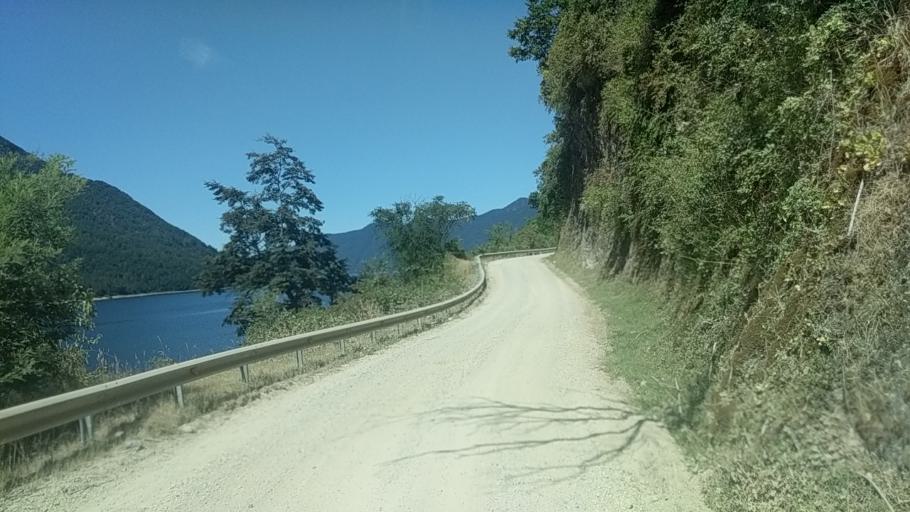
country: CL
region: Araucania
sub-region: Provincia de Cautin
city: Pucon
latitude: -39.0631
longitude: -71.7105
